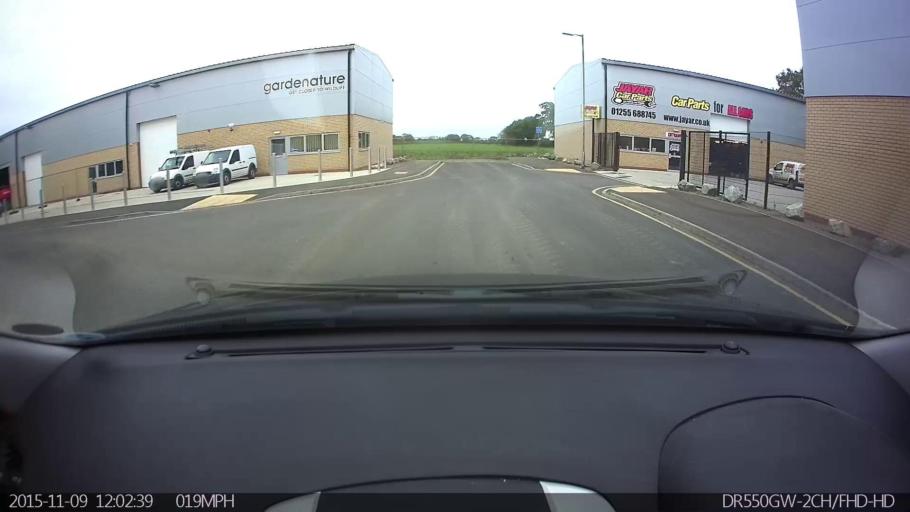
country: GB
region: England
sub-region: Essex
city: Little Clacton
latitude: 51.8202
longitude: 1.1666
